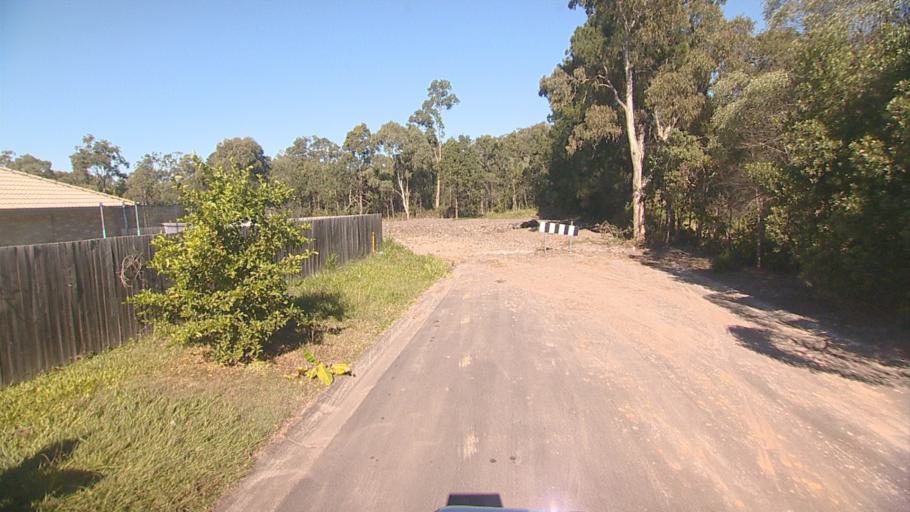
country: AU
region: Queensland
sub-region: Logan
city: Park Ridge South
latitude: -27.6714
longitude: 153.0202
